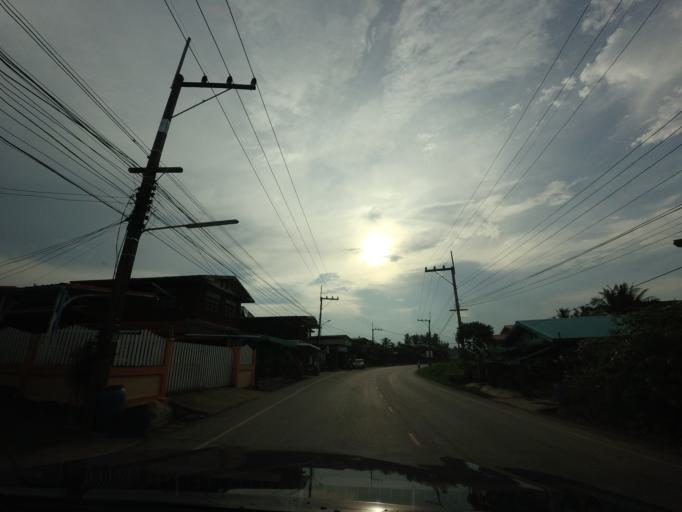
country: TH
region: Nong Khai
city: Pho Tak
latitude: 17.7795
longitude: 102.3912
